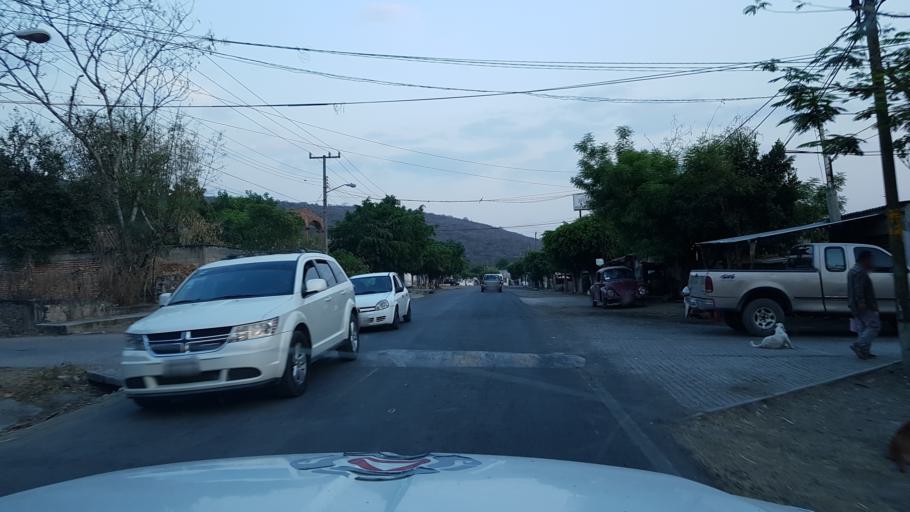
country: MX
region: Morelos
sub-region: Tlaltizapan de Zapata
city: Colonia Palo Prieto (Chipitongo)
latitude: 18.7128
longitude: -99.1089
